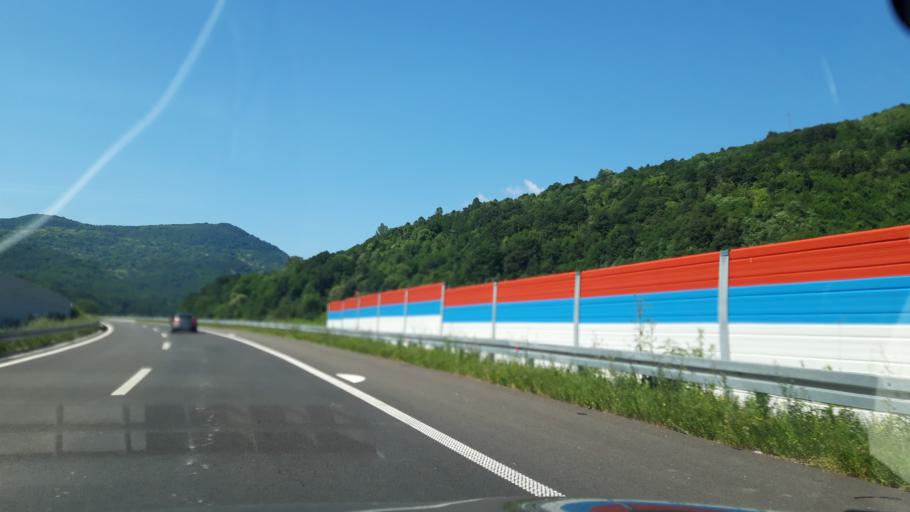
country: RS
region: Central Serbia
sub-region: Pcinjski Okrug
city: Vladicin Han
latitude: 42.7802
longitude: 22.0920
